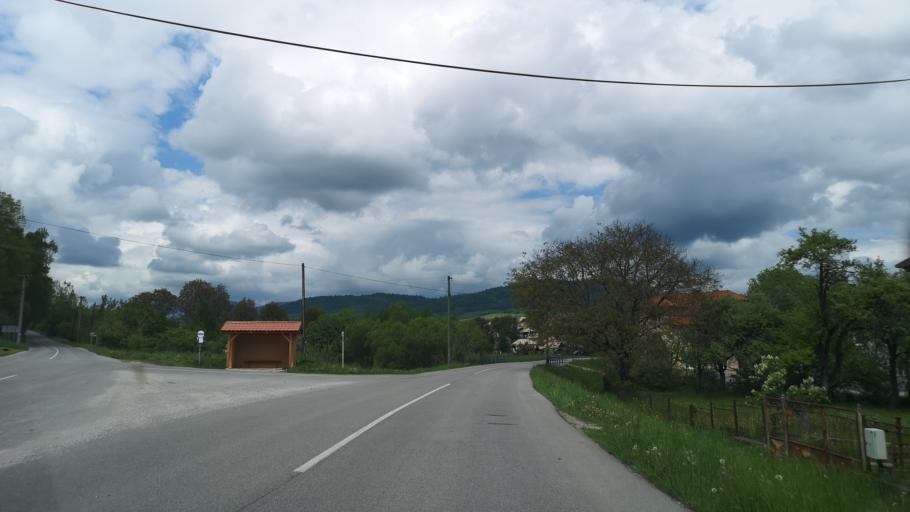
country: SK
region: Kosicky
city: Dobsina
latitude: 48.6911
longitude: 20.3470
